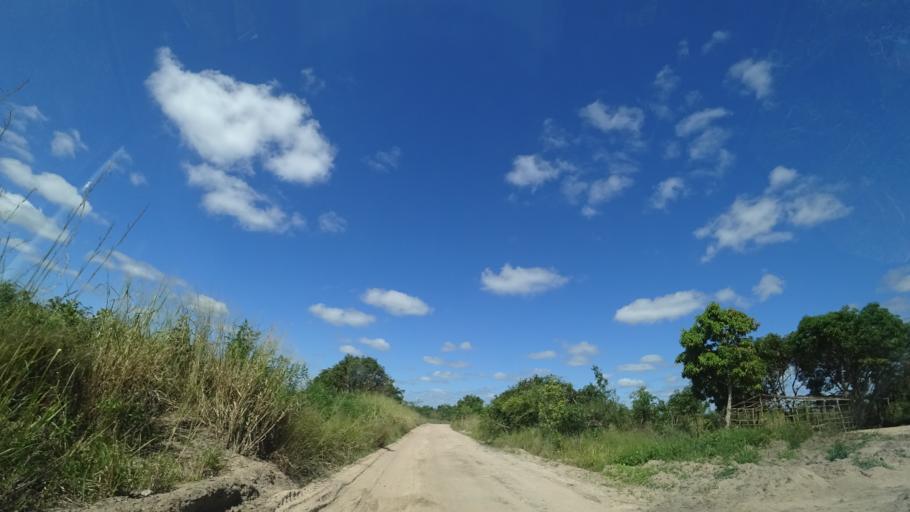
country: MZ
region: Sofala
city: Dondo
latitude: -19.2921
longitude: 34.6897
